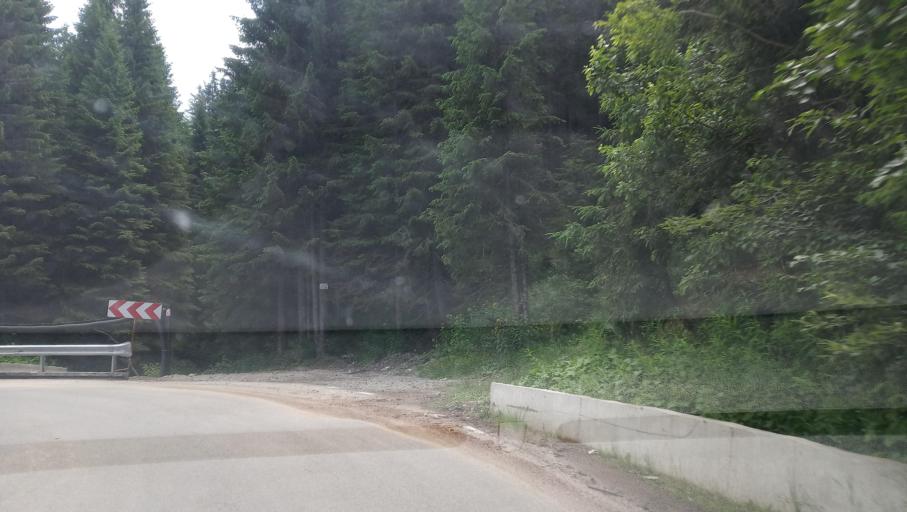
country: RO
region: Dambovita
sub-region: Comuna Moroeni
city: Glod
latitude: 45.3246
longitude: 25.4490
